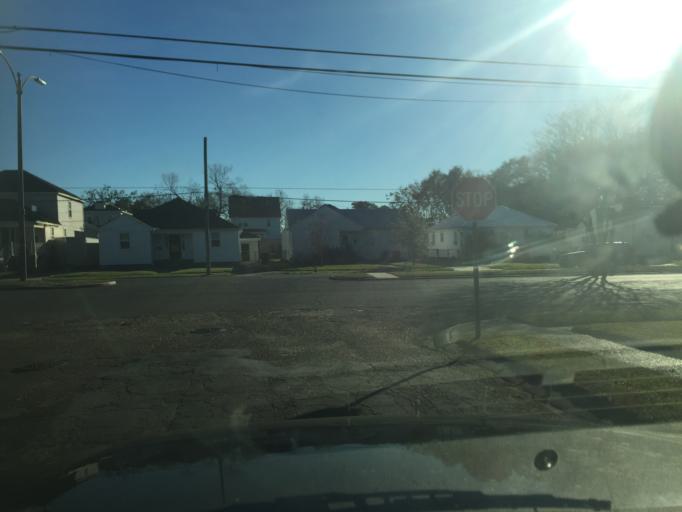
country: US
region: Louisiana
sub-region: Orleans Parish
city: New Orleans
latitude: 29.9889
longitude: -90.0771
